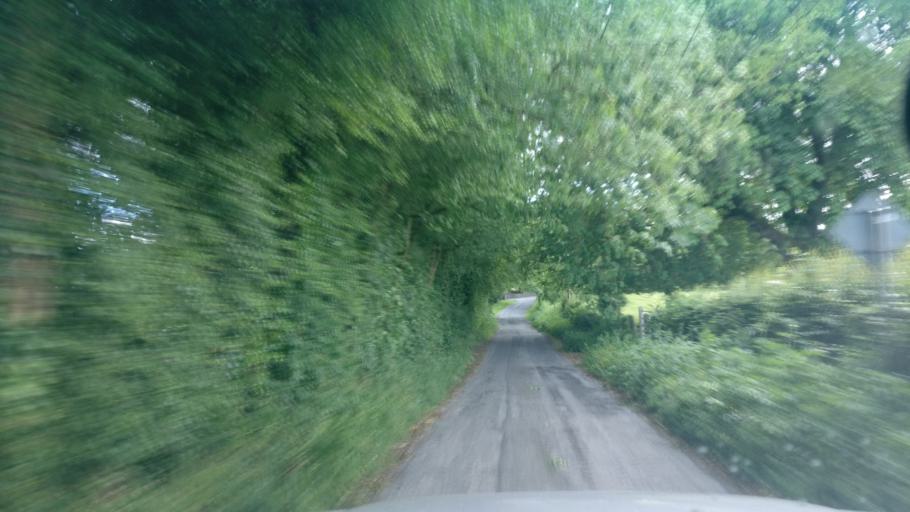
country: IE
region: Connaught
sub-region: County Galway
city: Ballinasloe
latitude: 53.2331
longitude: -8.2103
